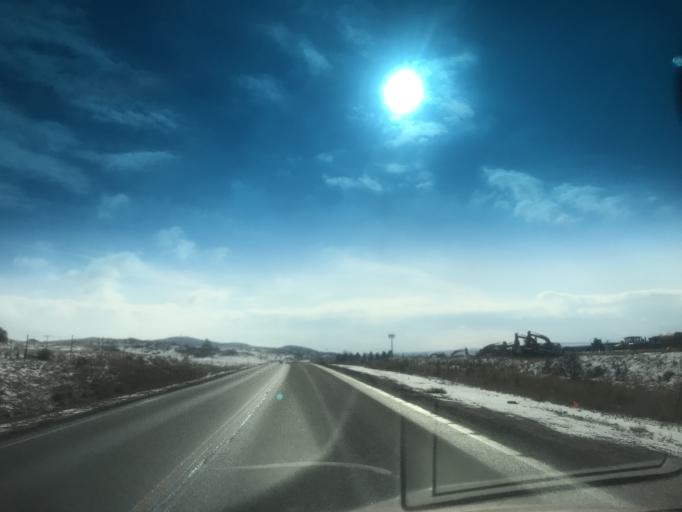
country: US
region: Colorado
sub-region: Douglas County
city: Highlands Ranch
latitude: 39.4756
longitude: -104.9911
